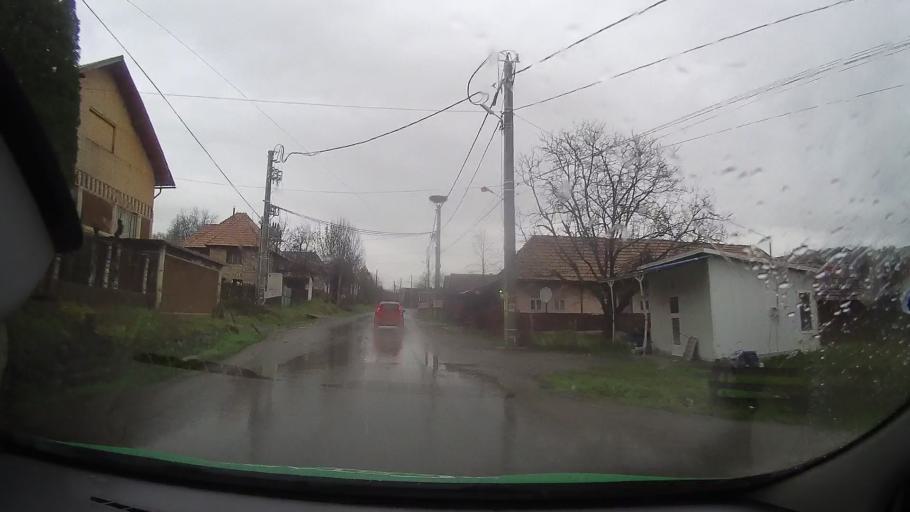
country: RO
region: Mures
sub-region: Comuna Vatava
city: Vatava
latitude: 46.9362
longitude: 24.7681
